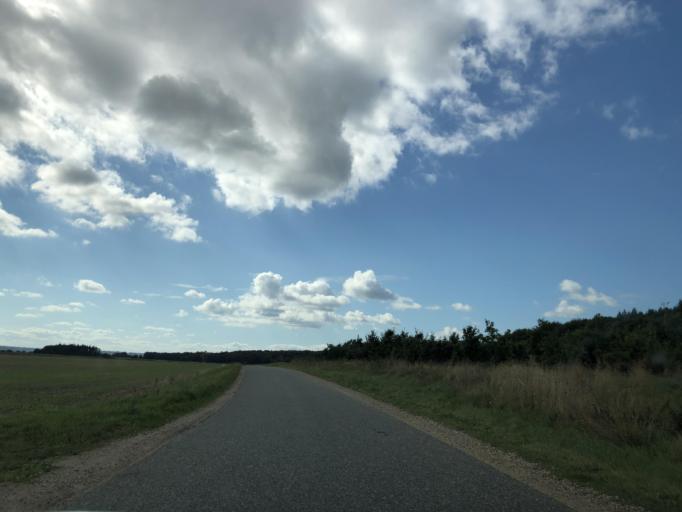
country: DK
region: Central Jutland
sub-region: Viborg Kommune
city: Viborg
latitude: 56.5725
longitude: 9.3409
